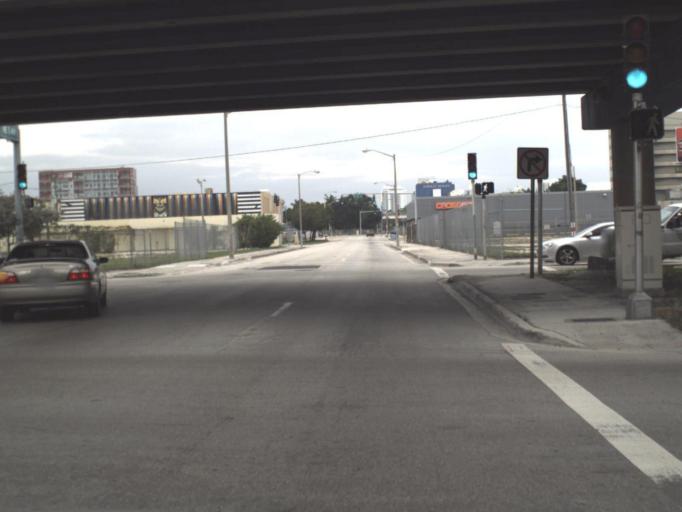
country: US
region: Florida
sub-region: Miami-Dade County
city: Miami
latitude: 25.7858
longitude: -80.1923
